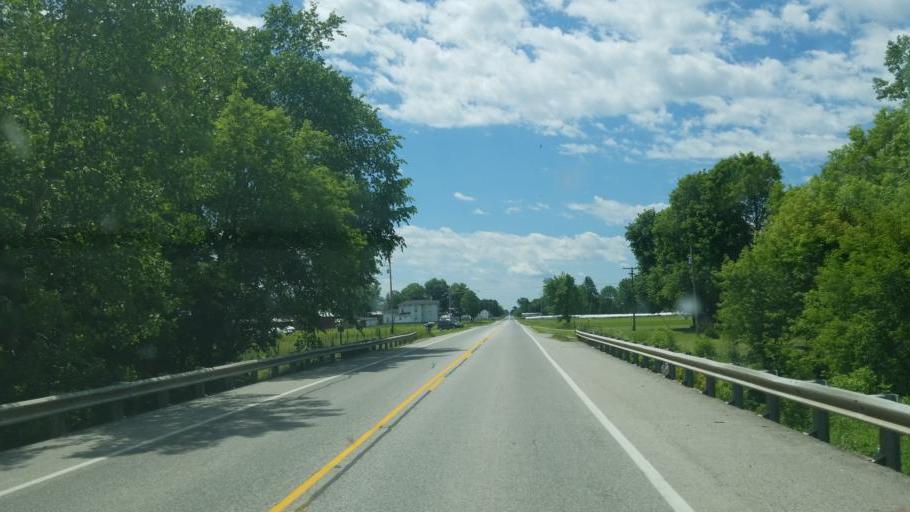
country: US
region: Ohio
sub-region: Geauga County
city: Middlefield
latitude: 41.4225
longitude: -80.9550
